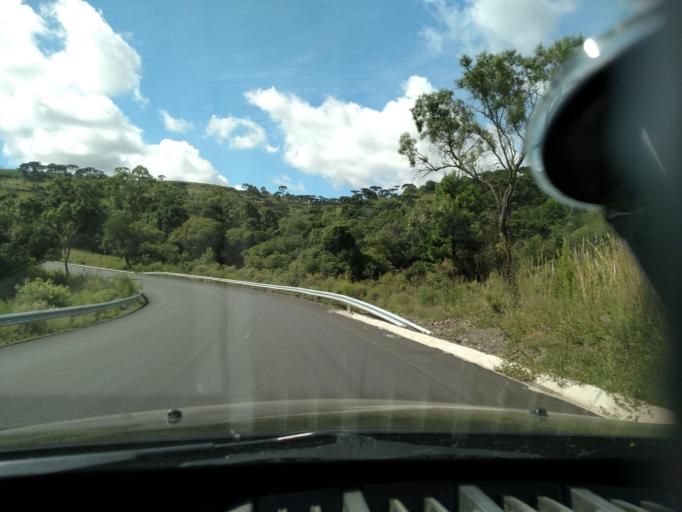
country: BR
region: Santa Catarina
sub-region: Sao Joaquim
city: Sao Joaquim
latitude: -28.1293
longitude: -50.0490
